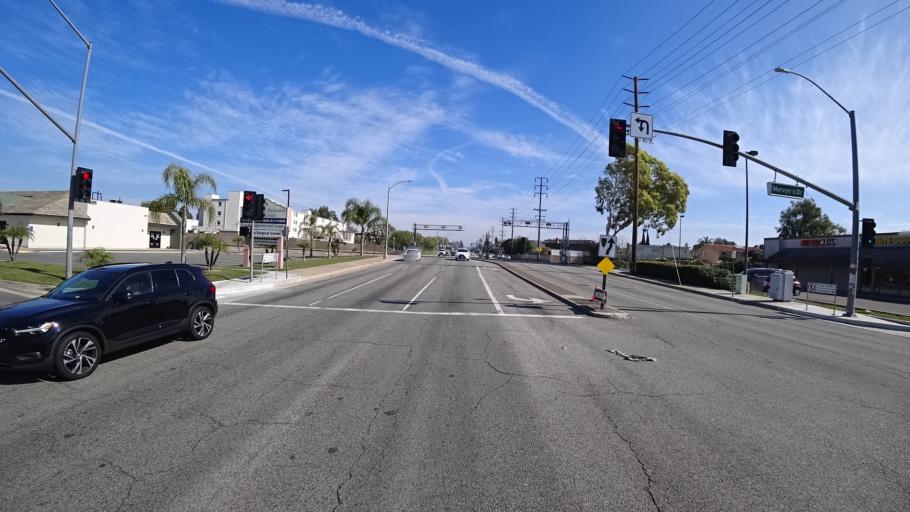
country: US
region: California
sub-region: Orange County
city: La Habra
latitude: 33.9174
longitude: -117.9295
